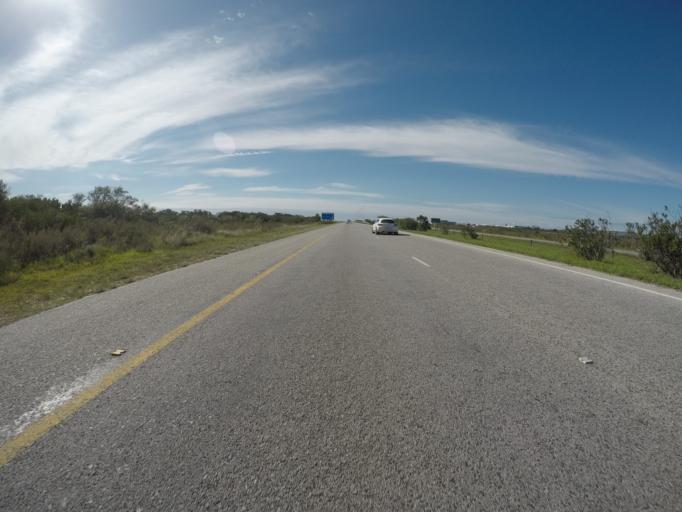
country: ZA
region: Eastern Cape
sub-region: Nelson Mandela Bay Metropolitan Municipality
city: Port Elizabeth
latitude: -33.9484
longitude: 25.4485
